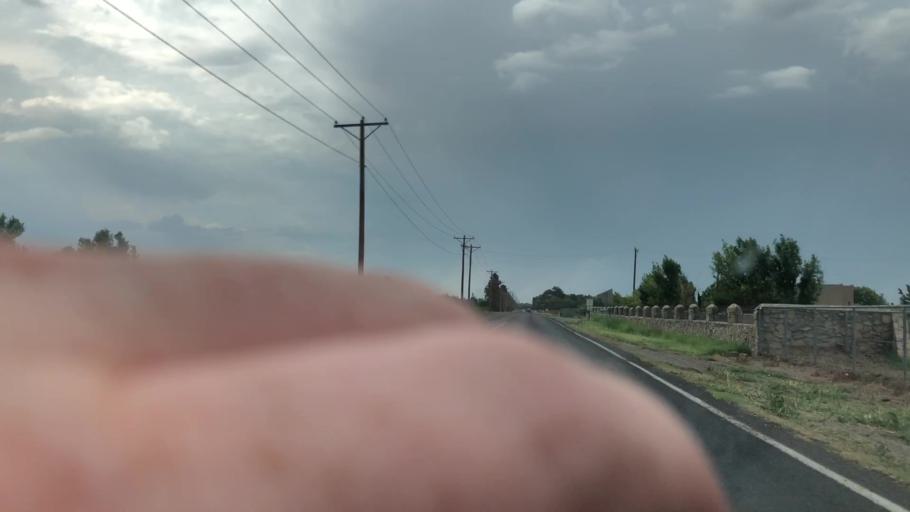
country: US
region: Texas
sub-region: El Paso County
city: Canutillo
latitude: 31.9214
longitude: -106.6268
